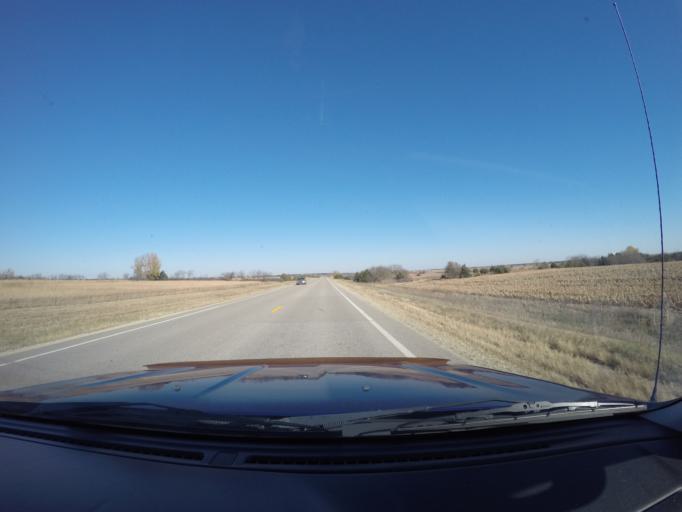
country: US
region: Kansas
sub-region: Riley County
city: Manhattan
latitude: 39.3693
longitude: -96.7565
